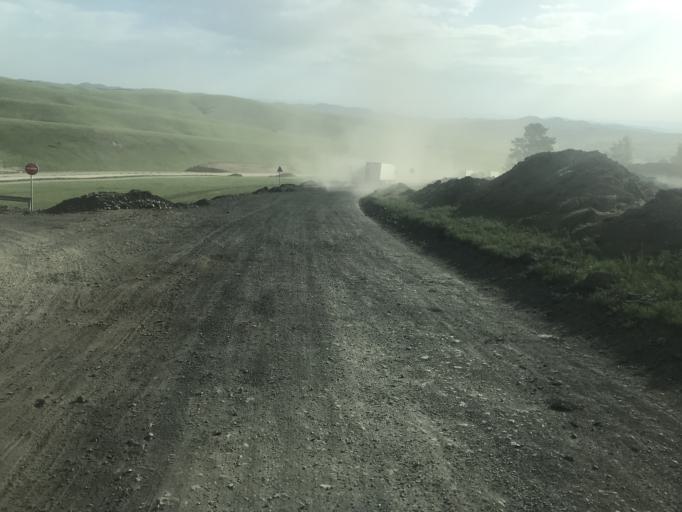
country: MN
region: Central Aimak
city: Javhlant
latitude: 48.6479
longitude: 106.0941
